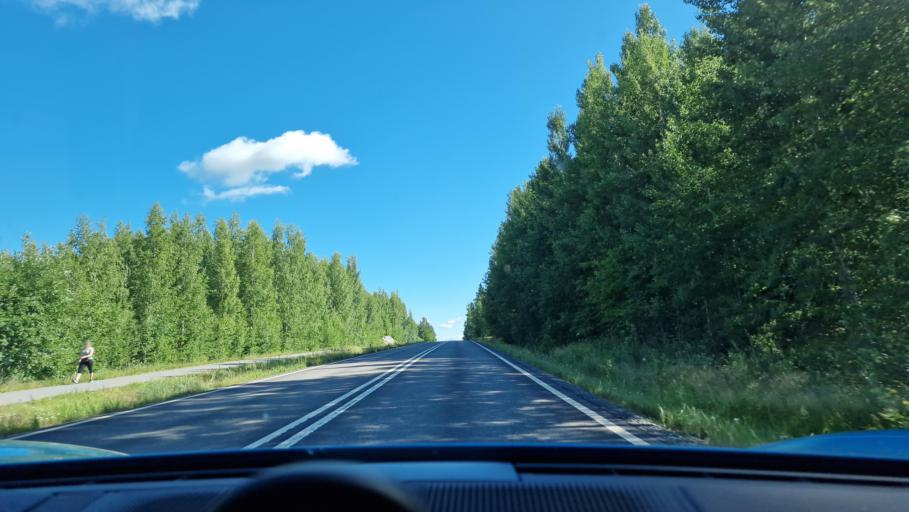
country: FI
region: Pirkanmaa
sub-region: Tampere
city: Kangasala
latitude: 61.4714
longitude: 24.1322
